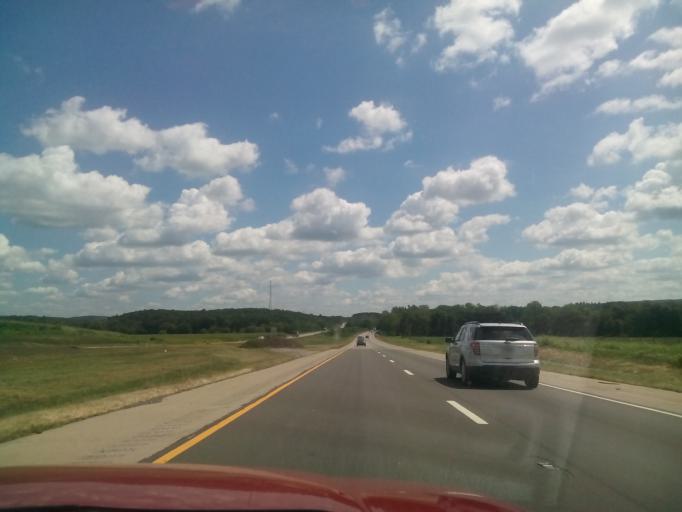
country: US
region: Pennsylvania
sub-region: Northumberland County
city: Milton
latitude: 41.0084
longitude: -76.7714
